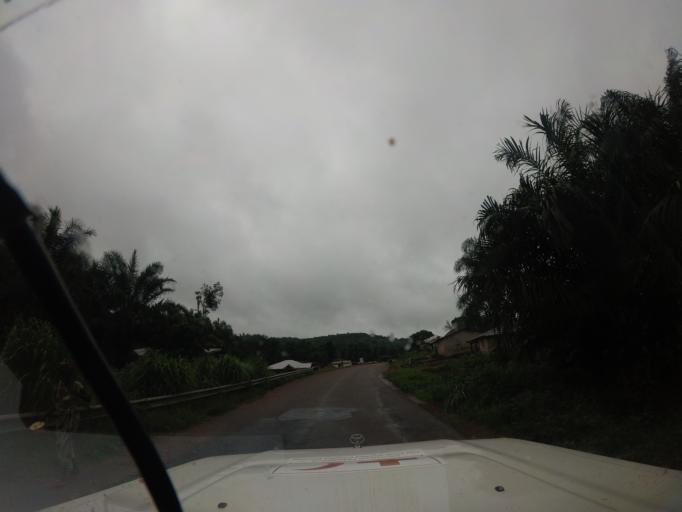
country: SL
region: Northern Province
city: Kabala
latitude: 9.3945
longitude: -11.7331
